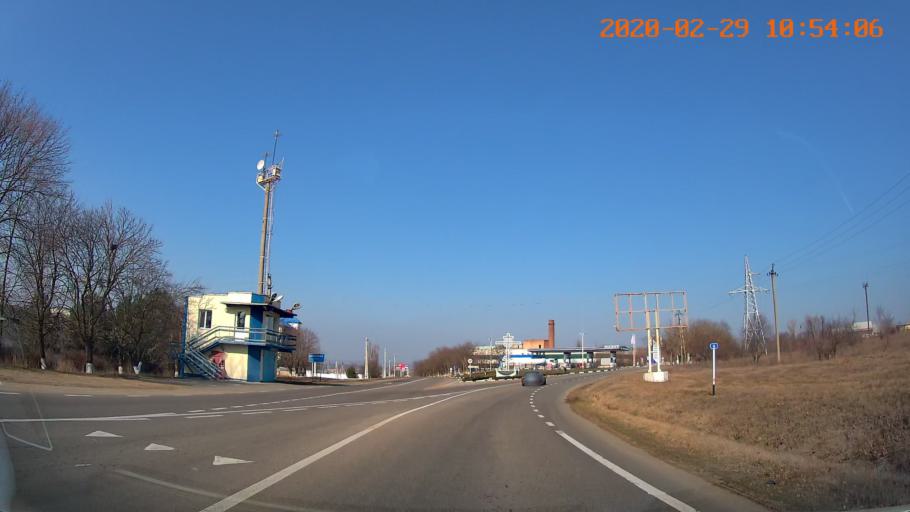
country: MD
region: Telenesti
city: Grigoriopol
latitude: 47.1200
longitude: 29.3283
